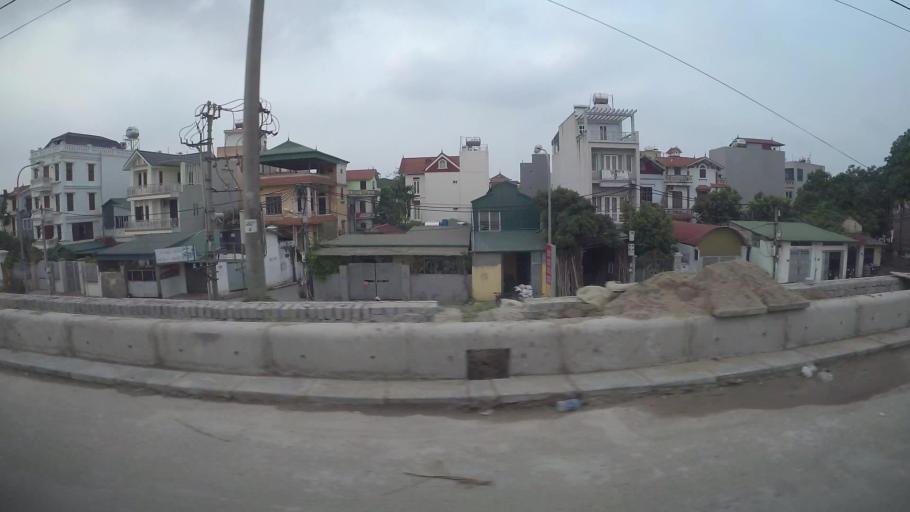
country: VN
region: Ha Noi
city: Trau Quy
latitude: 21.0213
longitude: 105.8971
